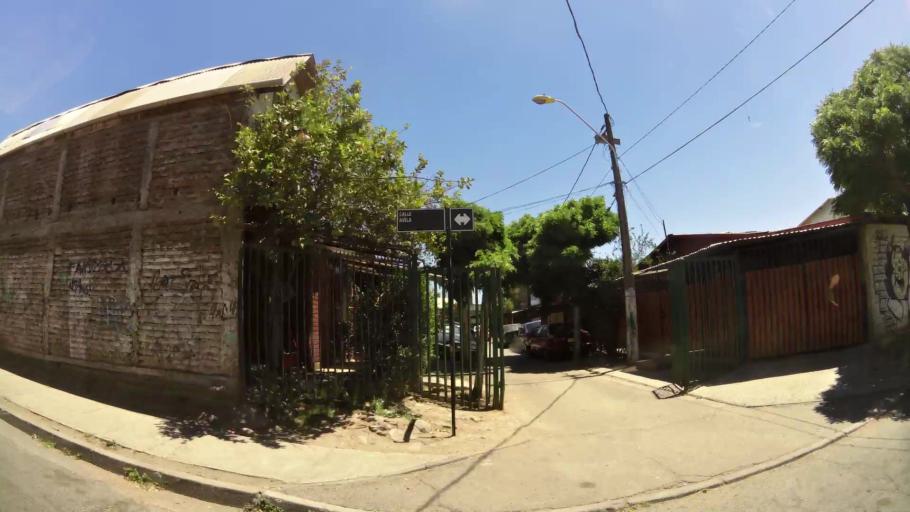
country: CL
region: Santiago Metropolitan
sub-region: Provincia de Maipo
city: San Bernardo
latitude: -33.5789
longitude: -70.6696
